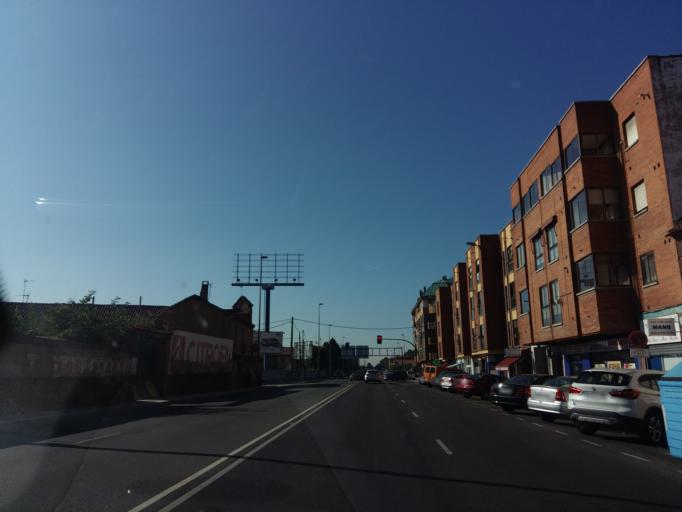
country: ES
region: Castille and Leon
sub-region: Provincia de Leon
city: Leon
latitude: 42.5832
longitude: -5.5841
